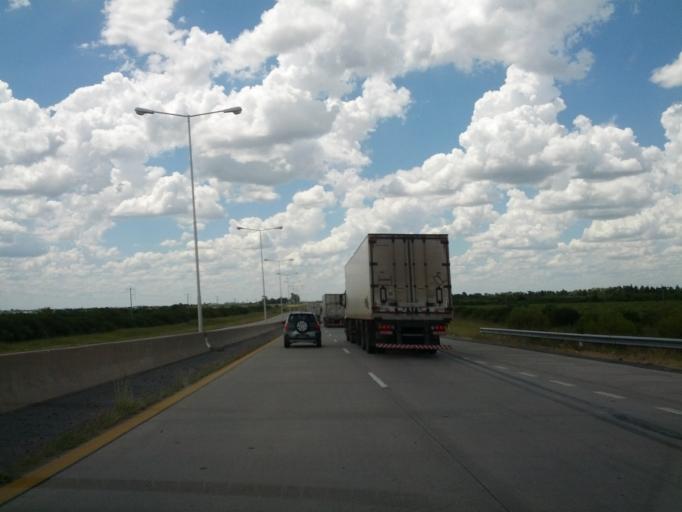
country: AR
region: Entre Rios
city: Gualeguaychu
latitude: -33.0100
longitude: -58.6061
